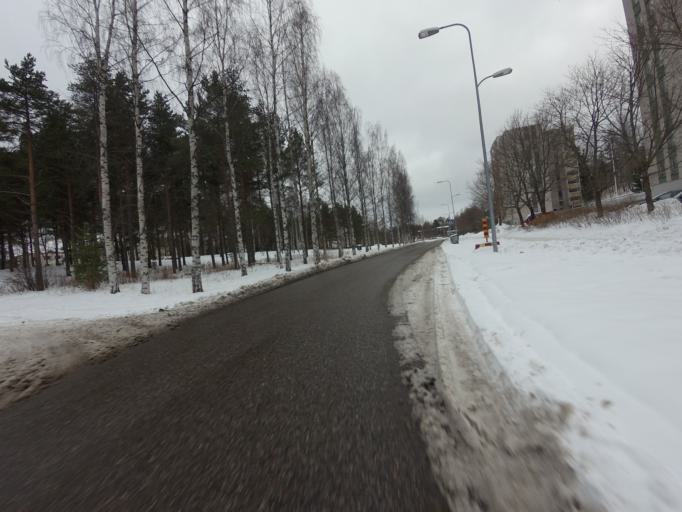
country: FI
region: Uusimaa
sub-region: Helsinki
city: Vantaa
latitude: 60.1813
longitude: 25.0586
